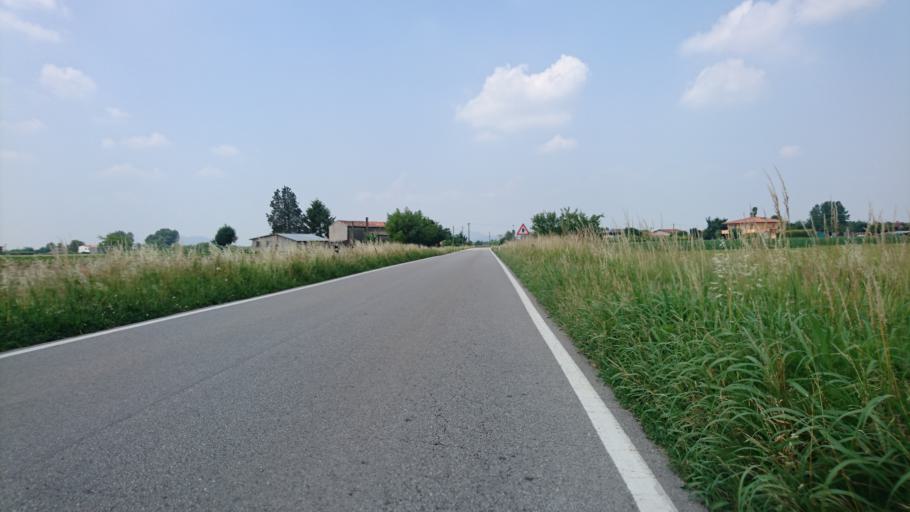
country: IT
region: Veneto
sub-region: Provincia di Padova
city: Terrassa Padovana
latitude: 45.2568
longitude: 11.8830
